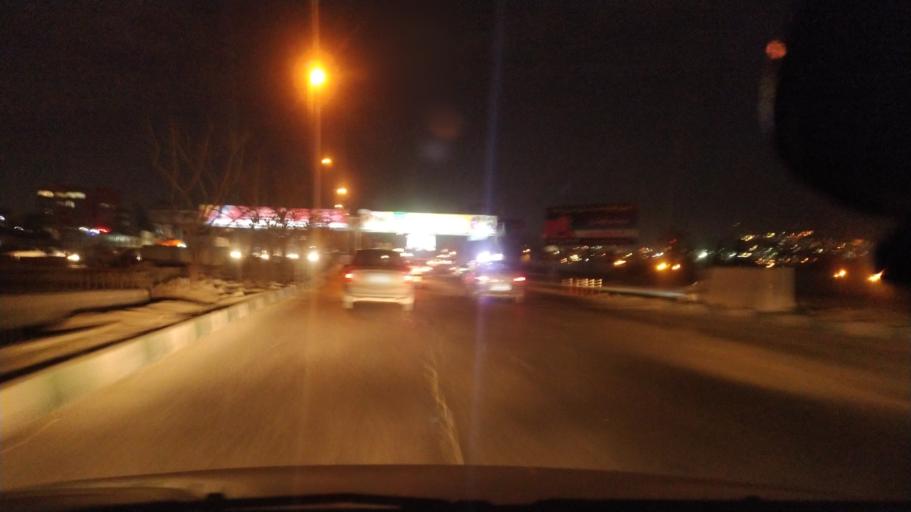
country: IR
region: Alborz
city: Karaj
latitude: 35.7921
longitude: 51.0035
